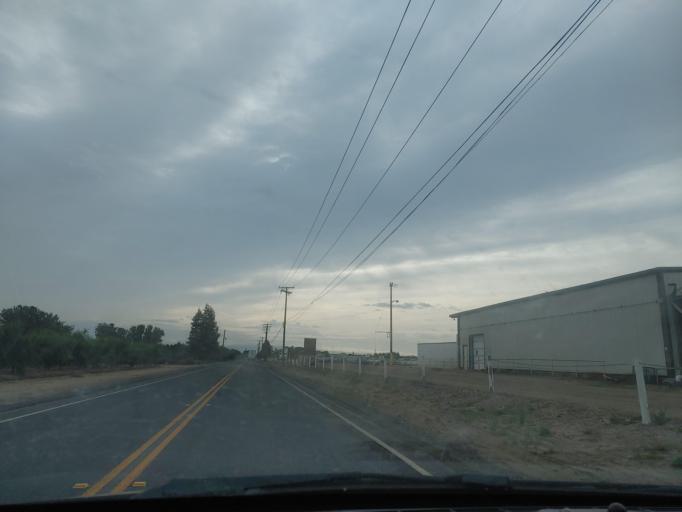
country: US
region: California
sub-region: Stanislaus County
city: Salida
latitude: 37.6817
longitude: -121.1115
